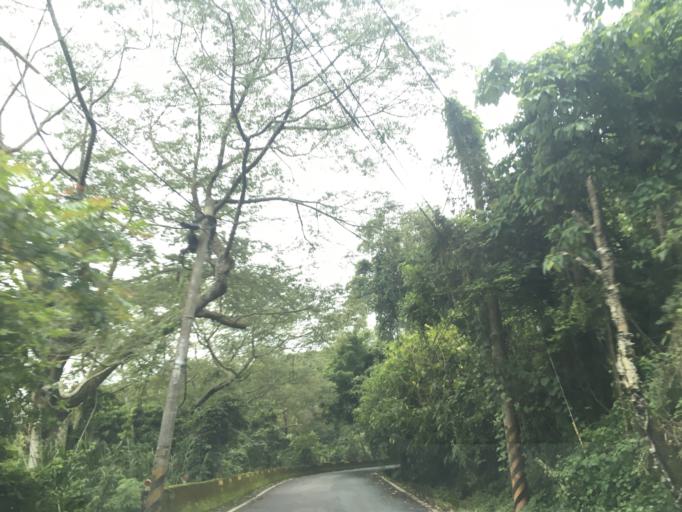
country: TW
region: Taiwan
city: Lugu
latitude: 23.5303
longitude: 120.7057
